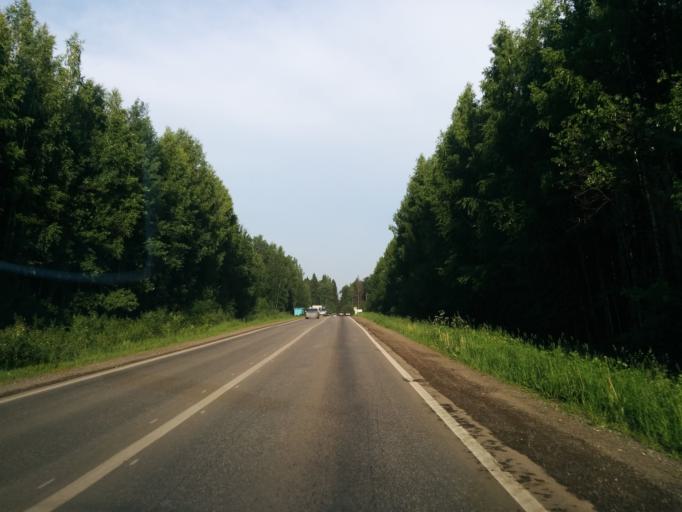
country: RU
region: Perm
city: Perm
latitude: 58.1356
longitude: 56.2981
